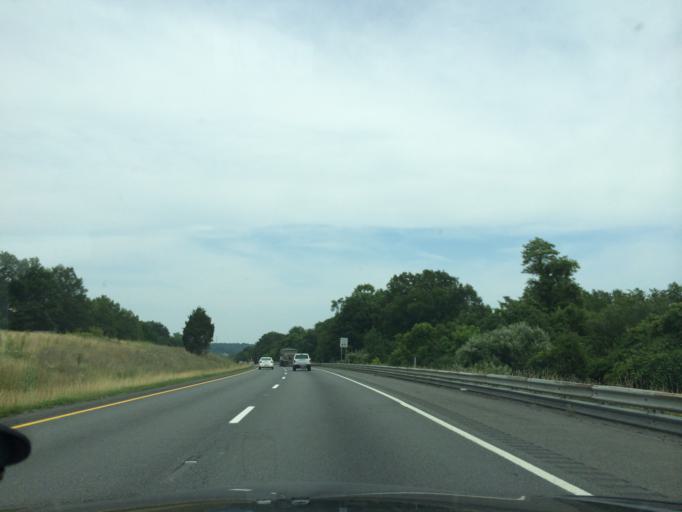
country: US
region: Maryland
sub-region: Washington County
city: Hancock
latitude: 39.6893
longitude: -78.1270
